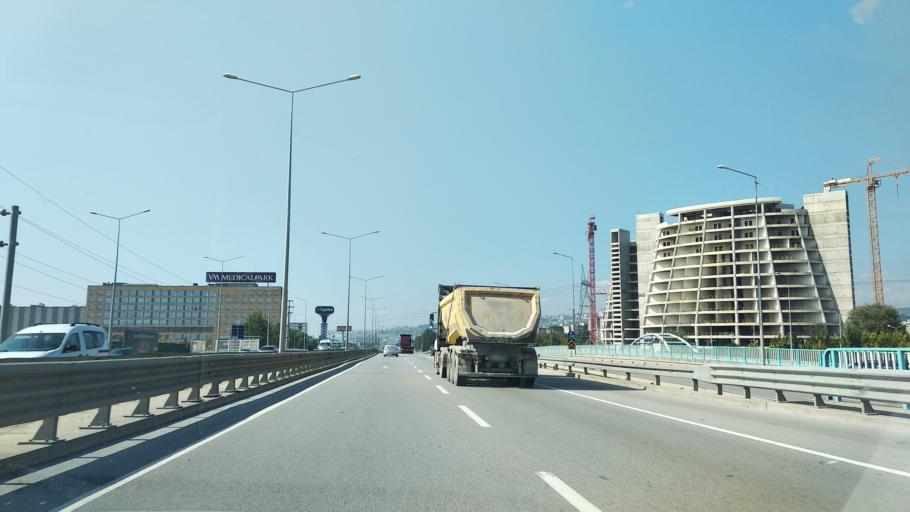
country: TR
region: Kocaeli
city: Kosekoy
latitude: 40.7589
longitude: 29.9854
